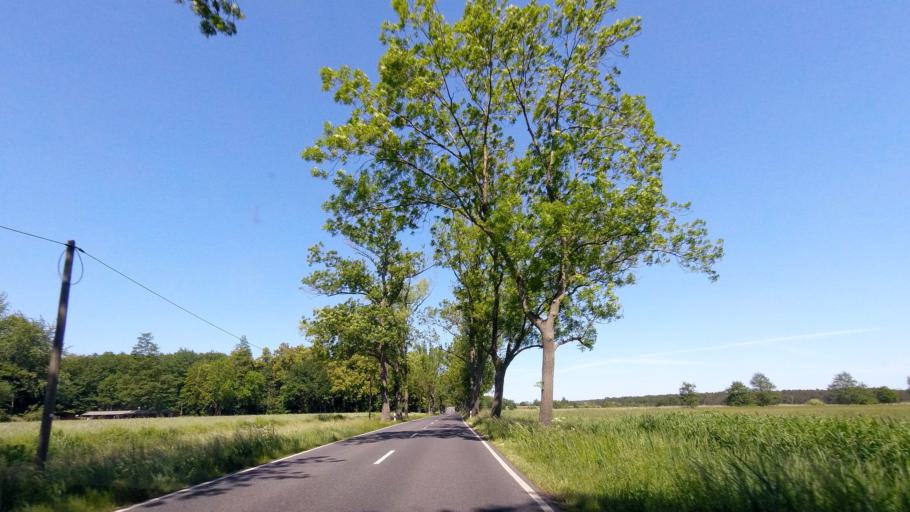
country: DE
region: Brandenburg
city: Ludwigsfelde
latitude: 52.2949
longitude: 13.2094
